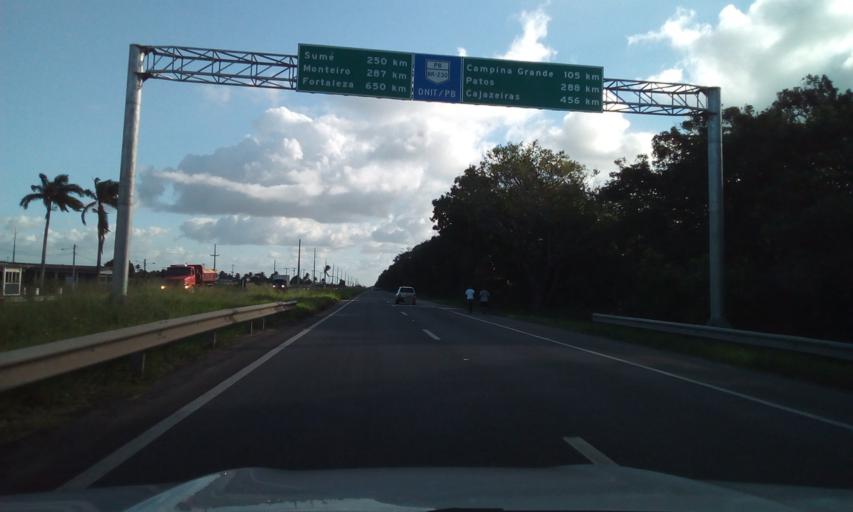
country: BR
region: Paraiba
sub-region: Santa Rita
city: Santa Rita
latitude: -7.1514
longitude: -35.0079
